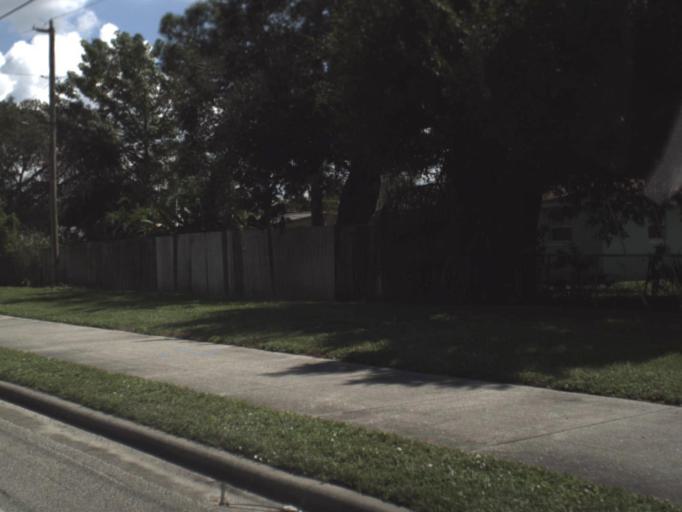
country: US
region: Florida
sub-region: Lee County
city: Palmona Park
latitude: 26.6820
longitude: -81.8917
